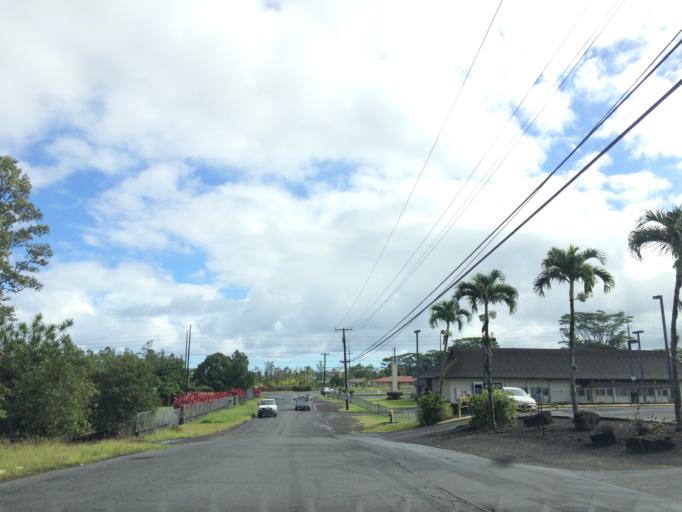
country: US
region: Hawaii
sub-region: Hawaii County
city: Orchidlands Estates
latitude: 19.5595
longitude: -154.9938
